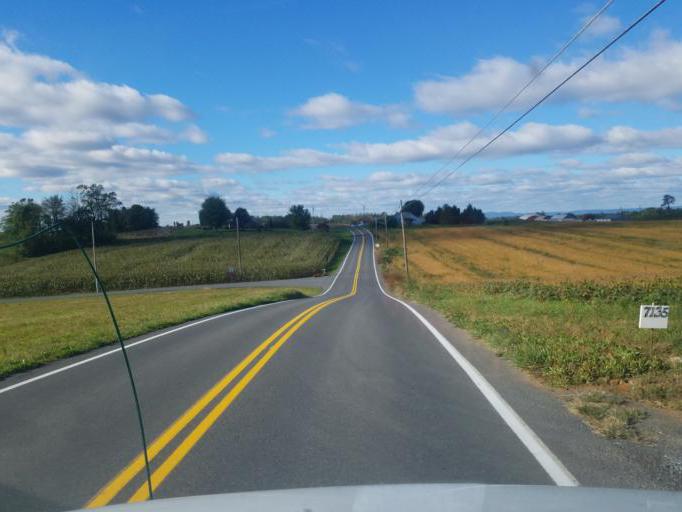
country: US
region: Pennsylvania
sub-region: Franklin County
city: Guilford Siding
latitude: 39.8327
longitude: -77.6310
